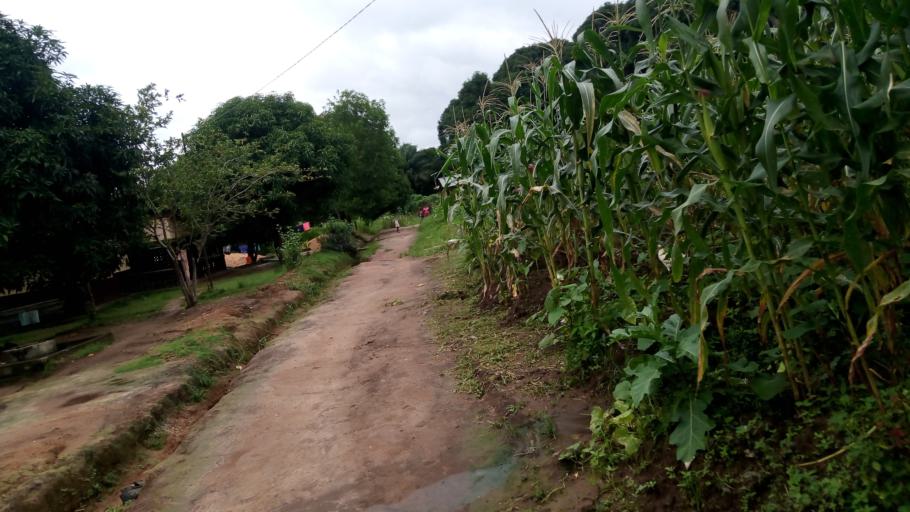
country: SL
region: Northern Province
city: Lunsar
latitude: 8.6918
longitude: -12.5332
